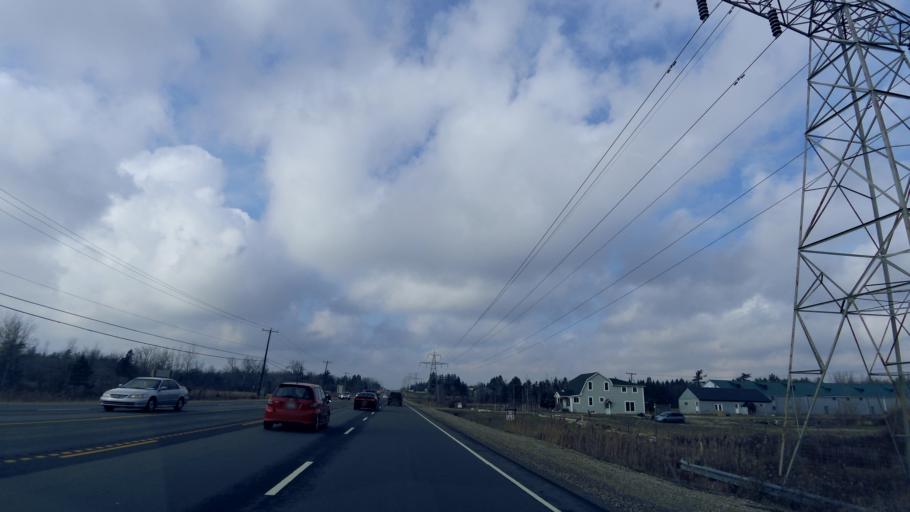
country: CA
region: Ontario
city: Ancaster
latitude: 43.3781
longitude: -80.0075
